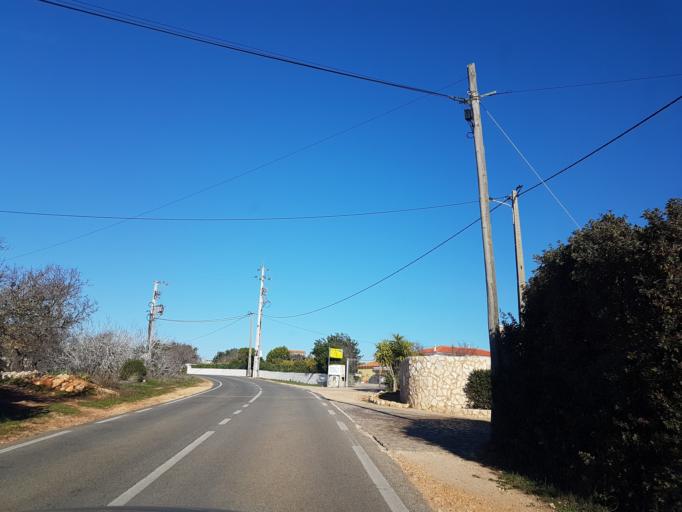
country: PT
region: Faro
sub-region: Lagoa
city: Carvoeiro
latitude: 37.0920
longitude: -8.4301
